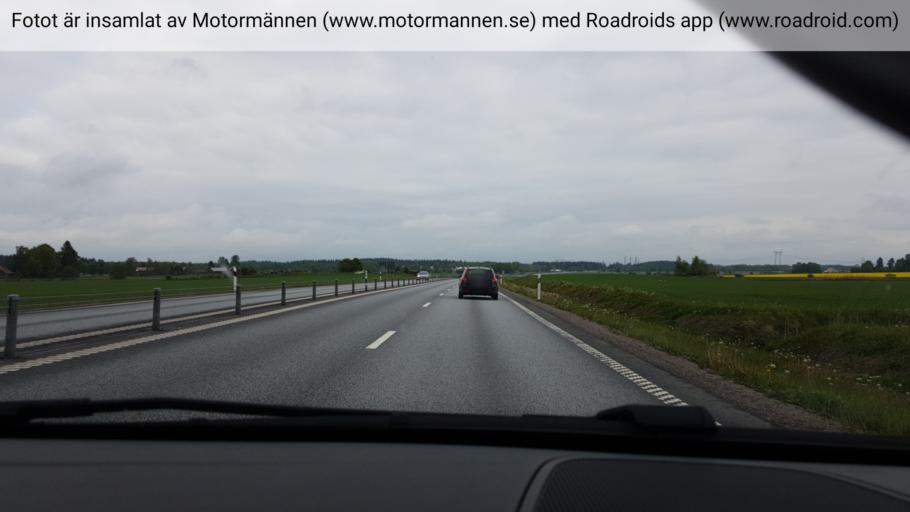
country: SE
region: Uppsala
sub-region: Osthammars Kommun
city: Osterbybruk
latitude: 60.0146
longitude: 17.9757
